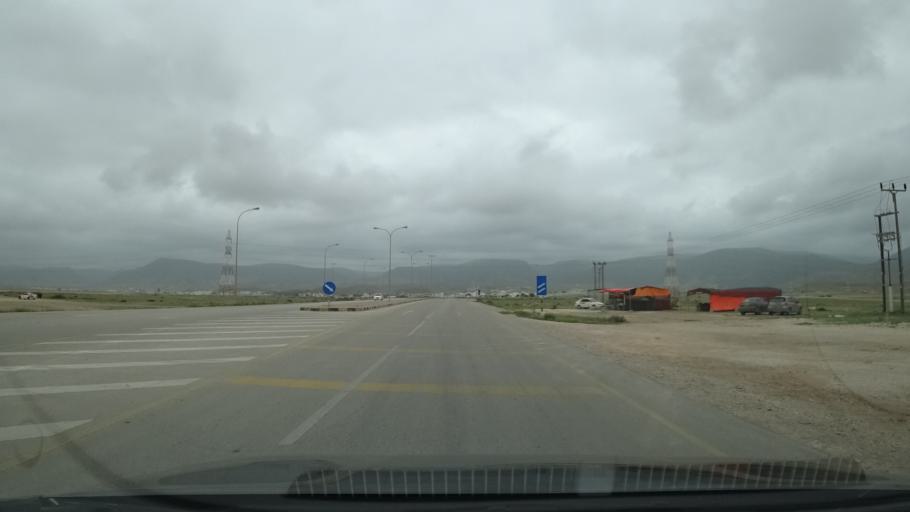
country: OM
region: Zufar
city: Salalah
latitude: 17.1011
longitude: 54.2167
